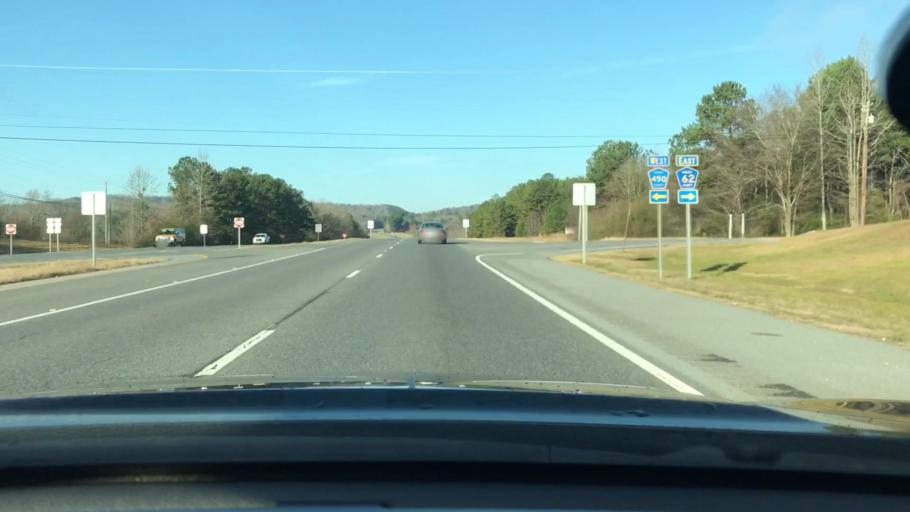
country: US
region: Alabama
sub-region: Shelby County
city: Harpersville
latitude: 33.3492
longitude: -86.4607
